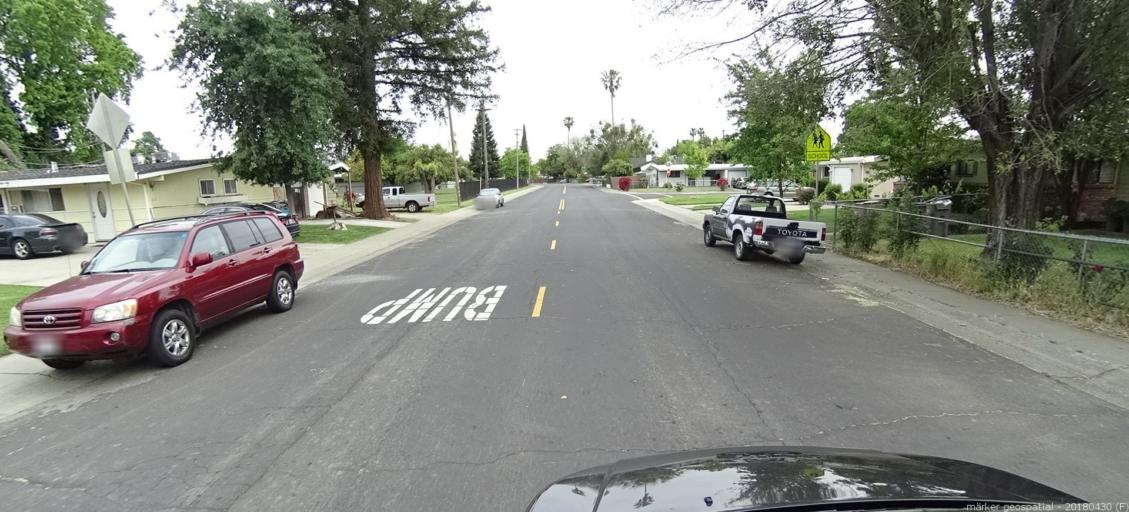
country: US
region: California
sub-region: Yolo County
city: West Sacramento
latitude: 38.5930
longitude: -121.5334
